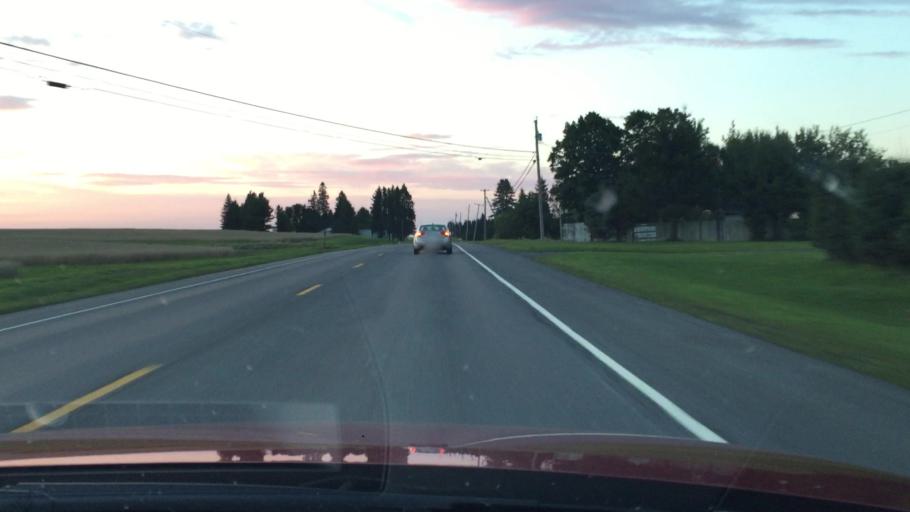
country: US
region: Maine
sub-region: Aroostook County
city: Easton
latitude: 46.5858
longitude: -67.9603
